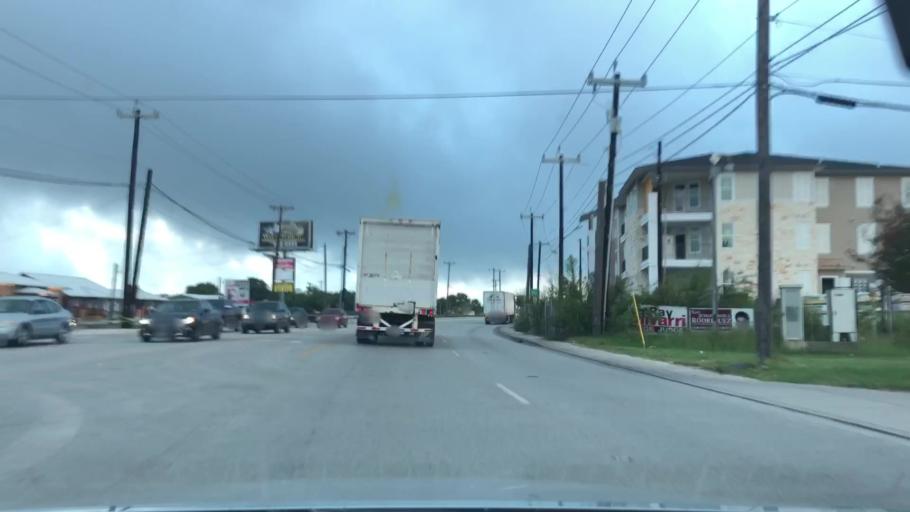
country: US
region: Texas
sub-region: Bexar County
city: Kirby
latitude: 29.4785
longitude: -98.3597
